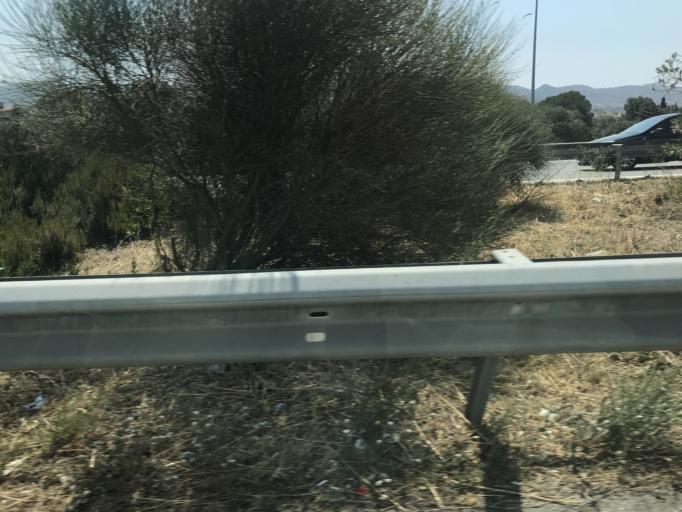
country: TR
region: Izmir
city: Urla
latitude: 38.3692
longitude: 26.8718
